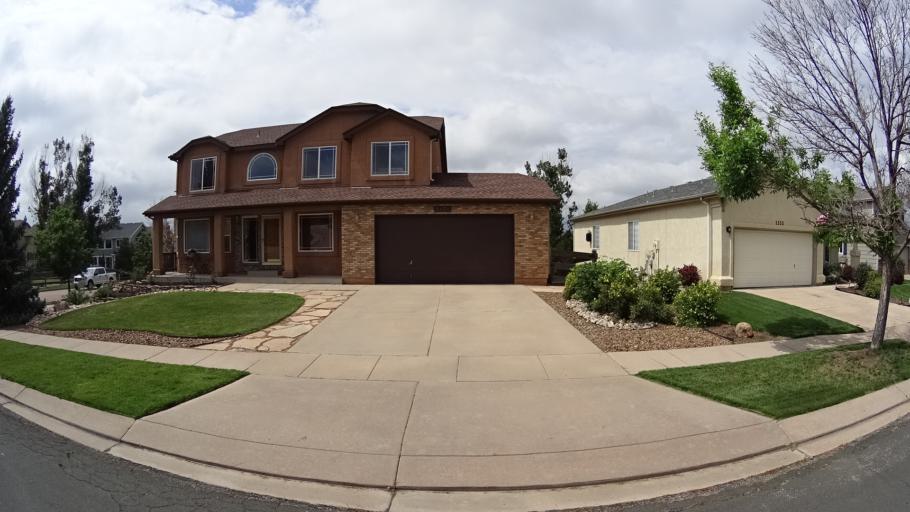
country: US
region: Colorado
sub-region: El Paso County
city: Gleneagle
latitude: 39.0105
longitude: -104.8022
